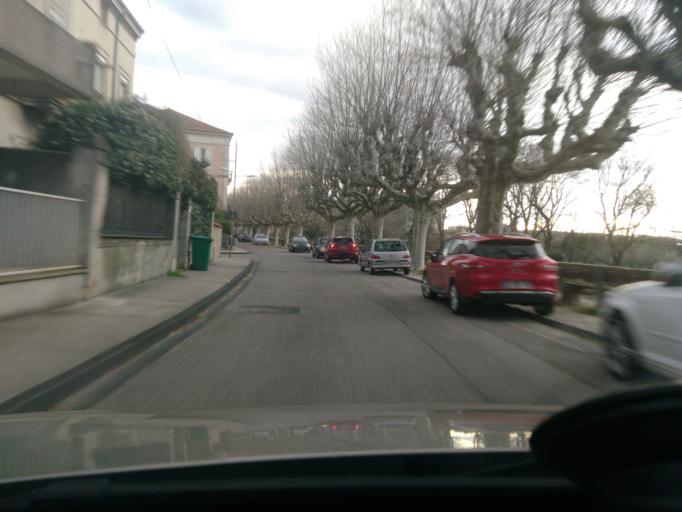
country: FR
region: Rhone-Alpes
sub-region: Departement de la Drome
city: Montelimar
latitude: 44.5528
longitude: 4.7492
